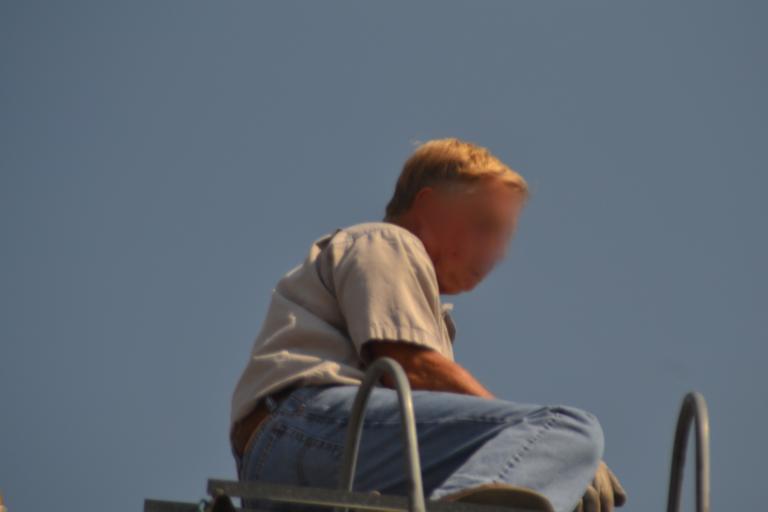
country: US
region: North Dakota
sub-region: Mercer County
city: Beulah
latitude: 47.6976
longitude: -101.9684
